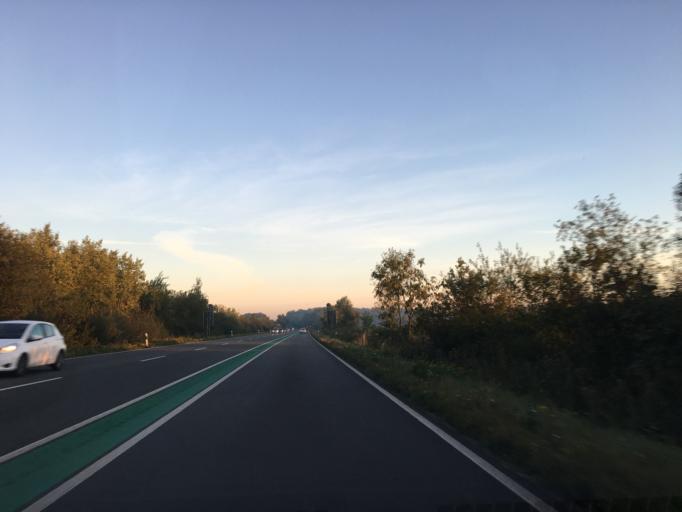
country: DE
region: North Rhine-Westphalia
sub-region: Regierungsbezirk Munster
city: Altenberge
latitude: 52.0840
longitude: 7.4176
